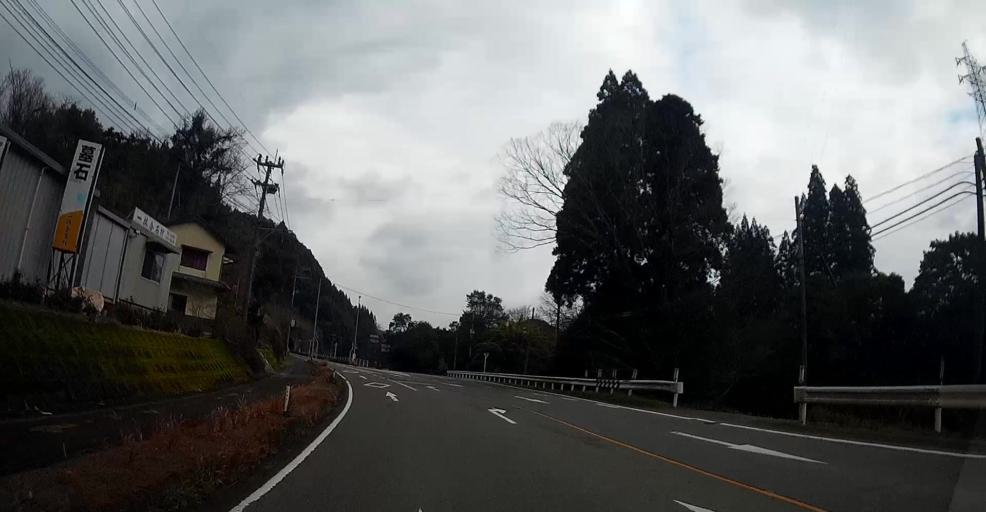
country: JP
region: Kumamoto
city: Matsubase
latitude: 32.6161
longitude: 130.8529
